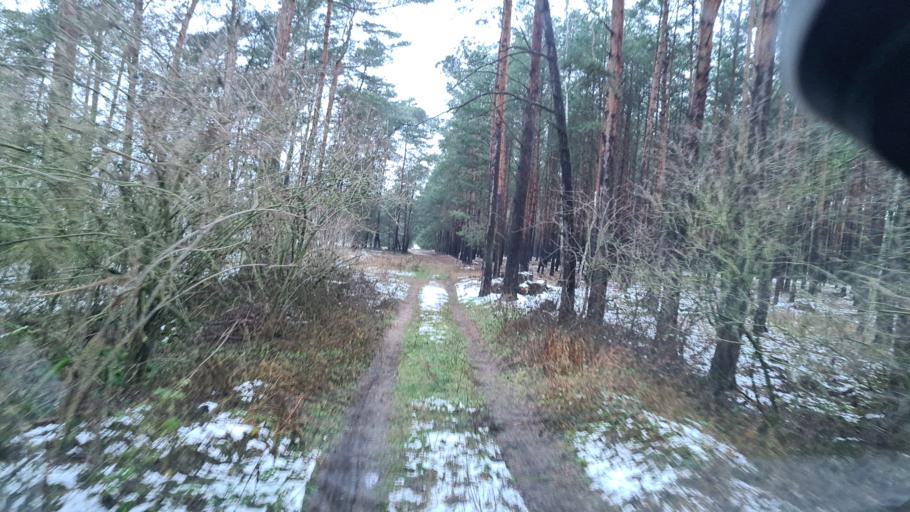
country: DE
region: Brandenburg
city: Schenkendobern
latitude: 51.9002
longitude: 14.5856
